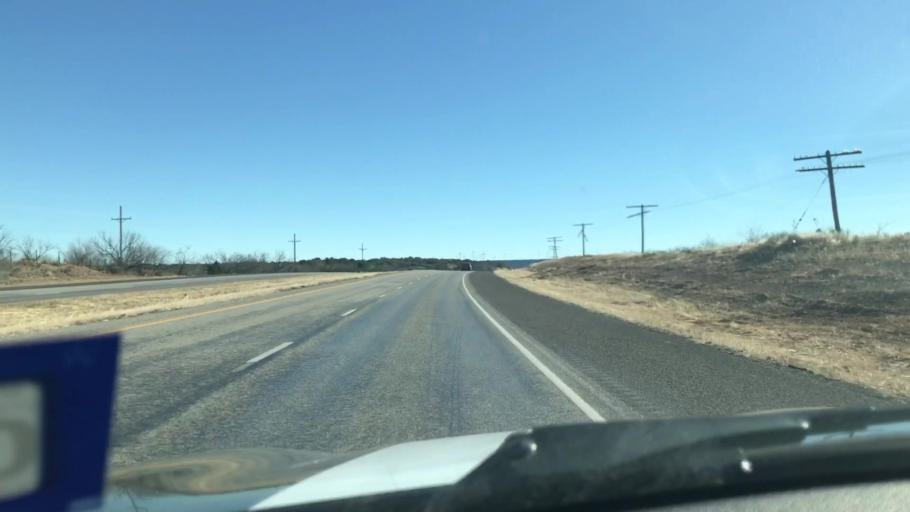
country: US
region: Texas
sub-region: Garza County
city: Post
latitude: 33.0271
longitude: -101.1855
